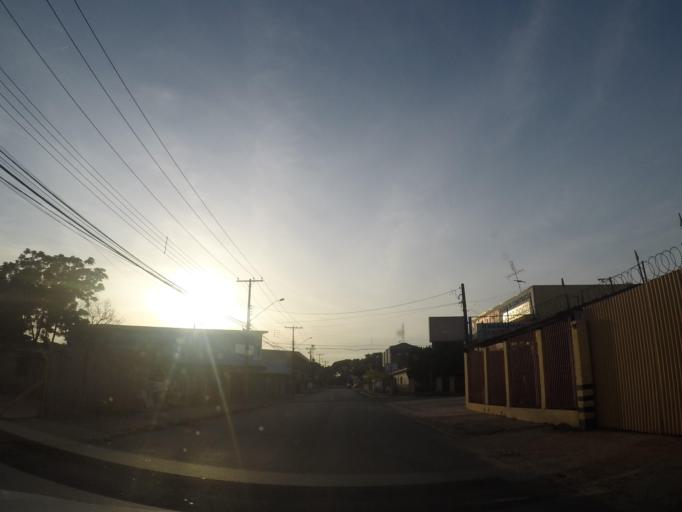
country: BR
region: Sao Paulo
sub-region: Hortolandia
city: Hortolandia
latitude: -22.8512
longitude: -47.1636
